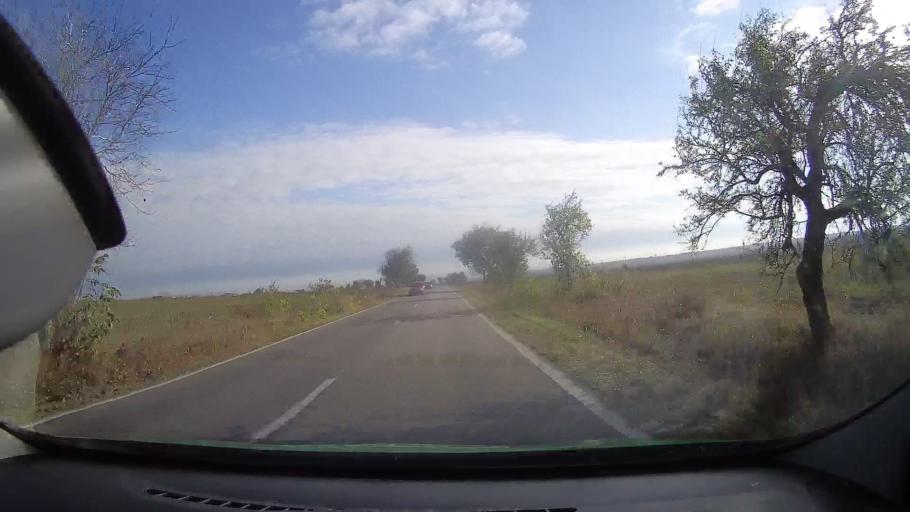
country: RO
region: Tulcea
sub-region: Comuna Mahmudia
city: Mahmudia
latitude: 45.0774
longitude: 29.0702
